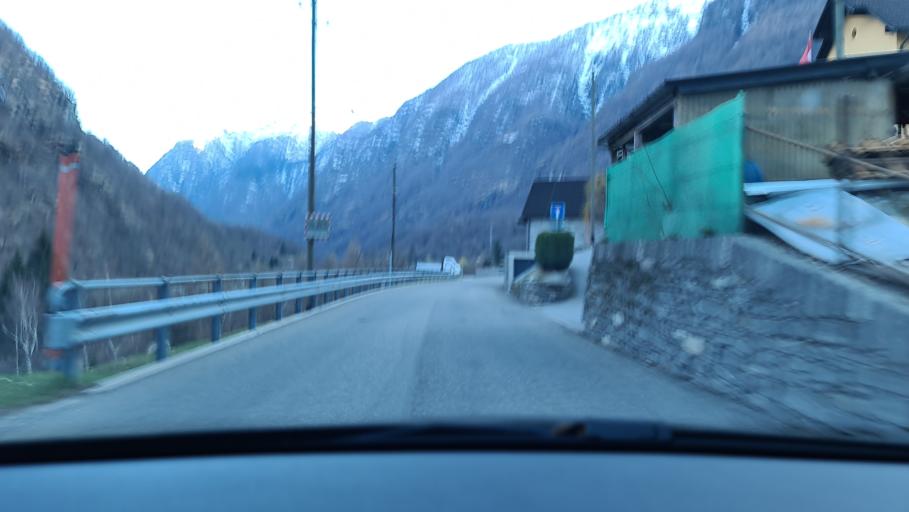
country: CH
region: Ticino
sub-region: Locarno District
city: Lavertezzo
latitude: 46.2998
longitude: 8.7926
